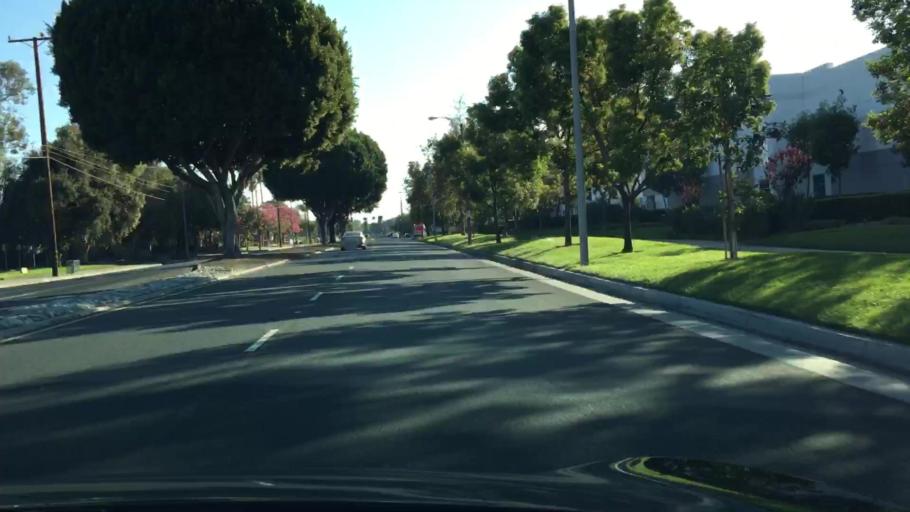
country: US
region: California
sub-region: Los Angeles County
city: Pico Rivera
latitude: 33.9796
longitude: -118.0998
